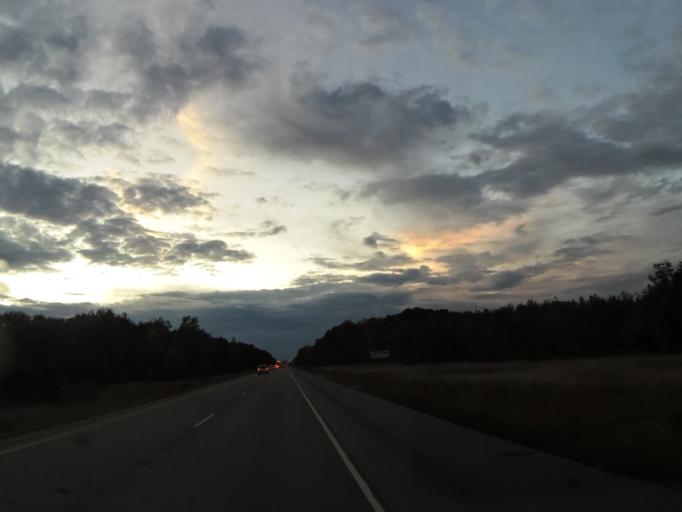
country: US
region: Wisconsin
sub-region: Monroe County
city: Tomah
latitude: 43.9506
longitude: -90.3333
